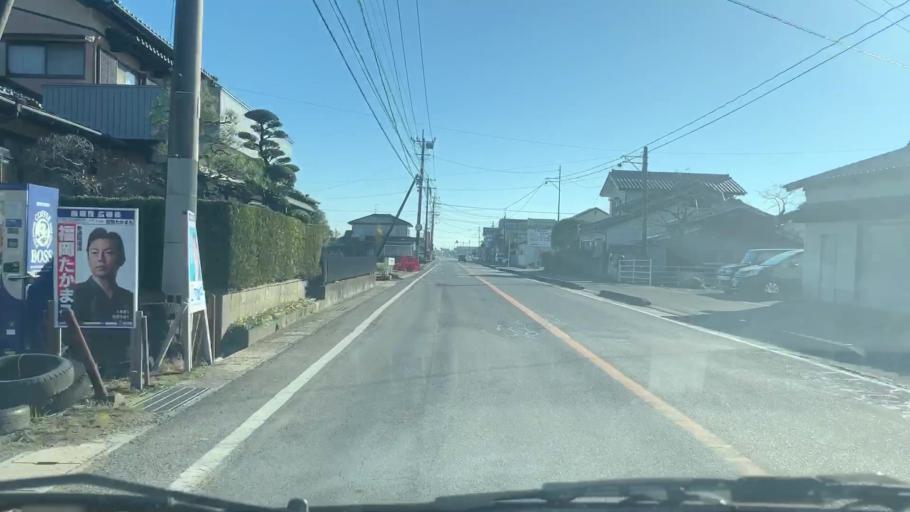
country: JP
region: Saga Prefecture
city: Kashima
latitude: 33.1834
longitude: 130.1727
